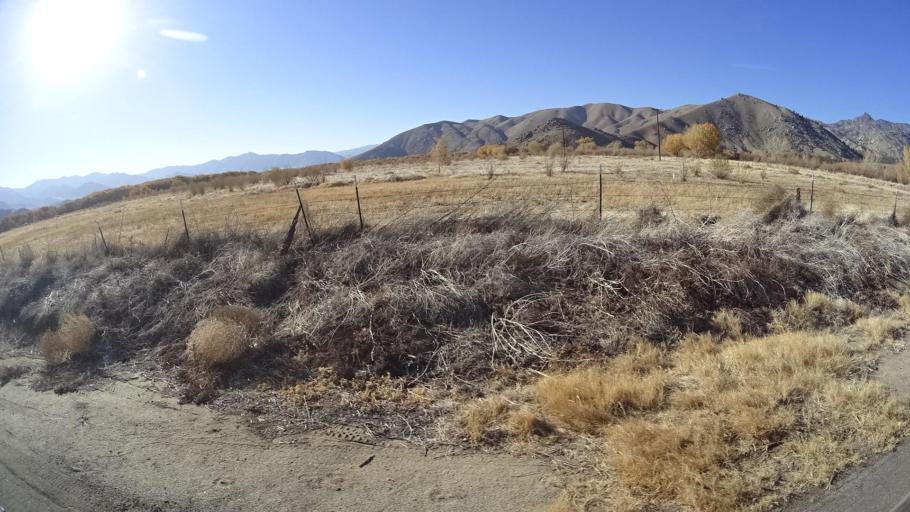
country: US
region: California
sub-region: Kern County
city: Weldon
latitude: 35.6813
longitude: -118.2901
